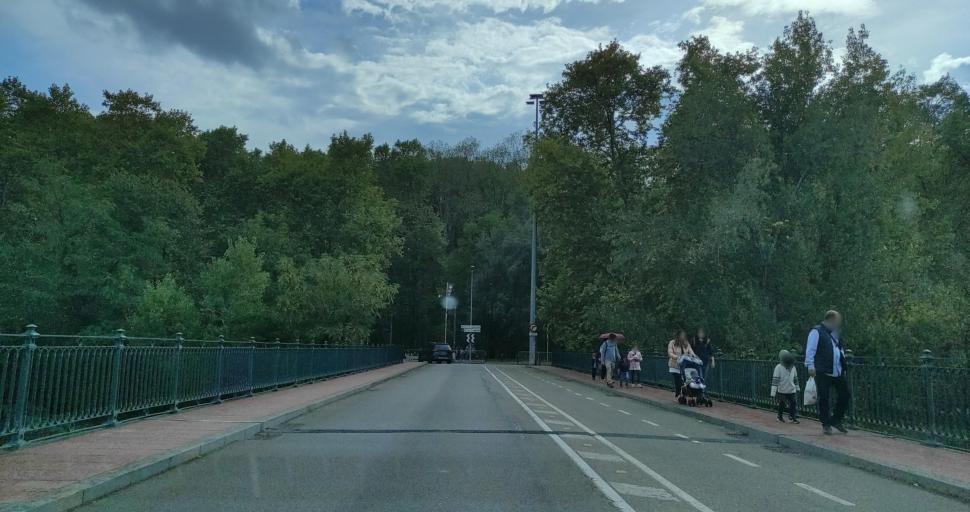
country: ES
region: Catalonia
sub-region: Provincia de Girona
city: Girona
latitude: 41.9904
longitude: 2.8191
